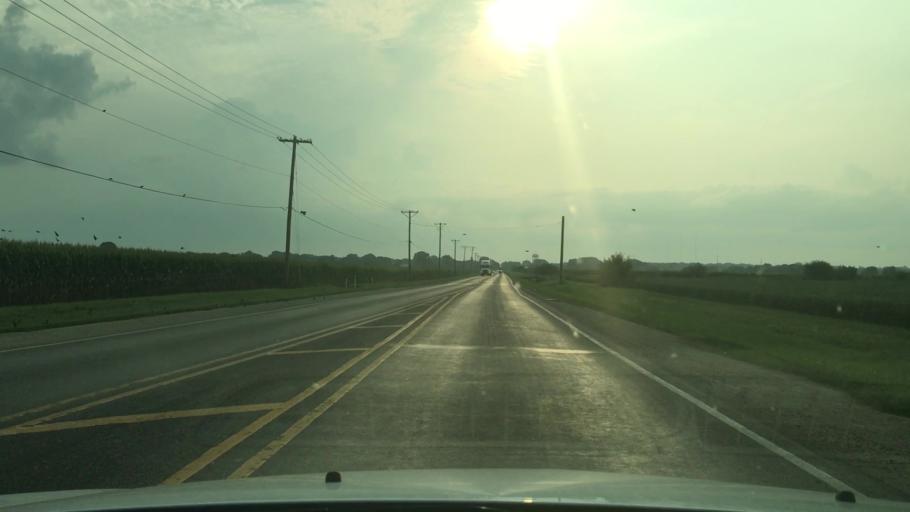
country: US
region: Illinois
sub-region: Ogle County
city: Rochelle
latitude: 41.9199
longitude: -89.0363
